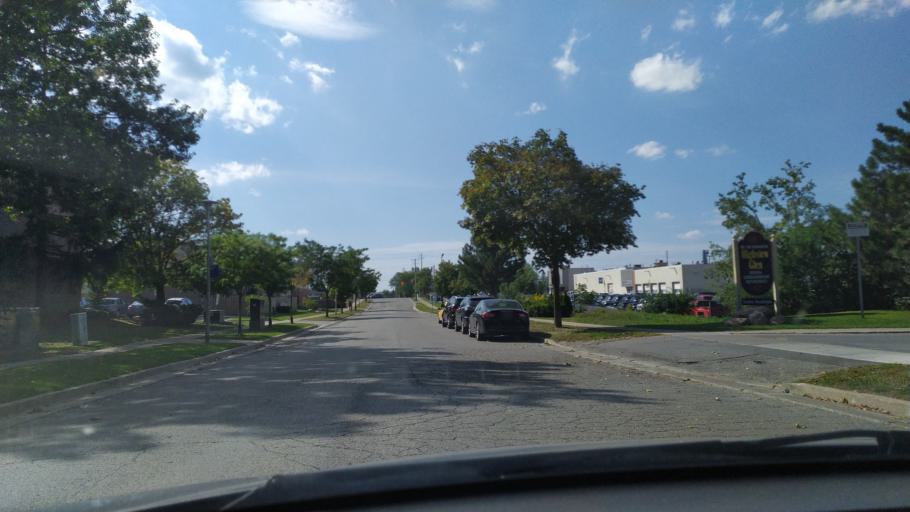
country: CA
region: Ontario
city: London
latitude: 42.9540
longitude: -81.2569
